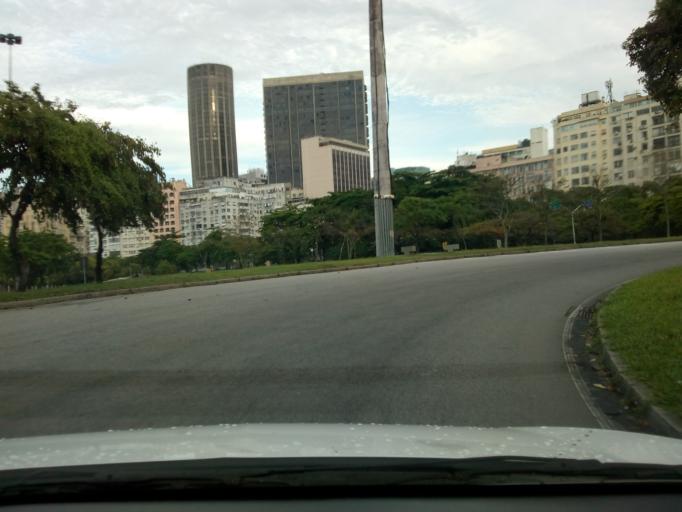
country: BR
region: Rio de Janeiro
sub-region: Rio De Janeiro
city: Rio de Janeiro
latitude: -22.9123
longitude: -43.1696
